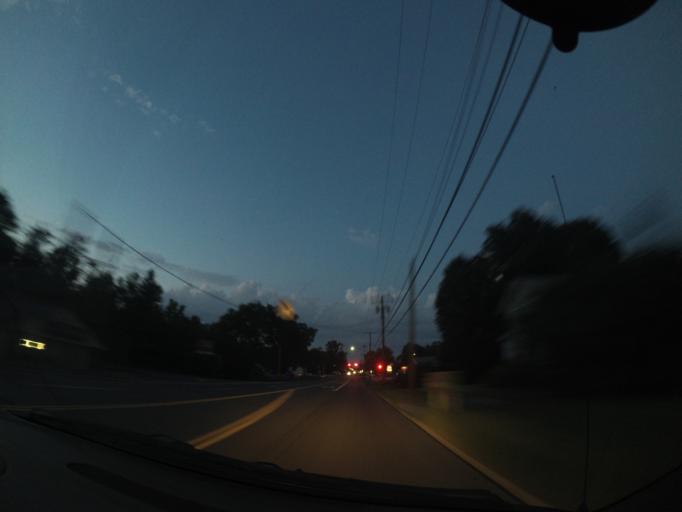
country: US
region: Ohio
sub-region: Ashtabula County
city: Ashtabula
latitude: 41.8350
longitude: -80.8570
